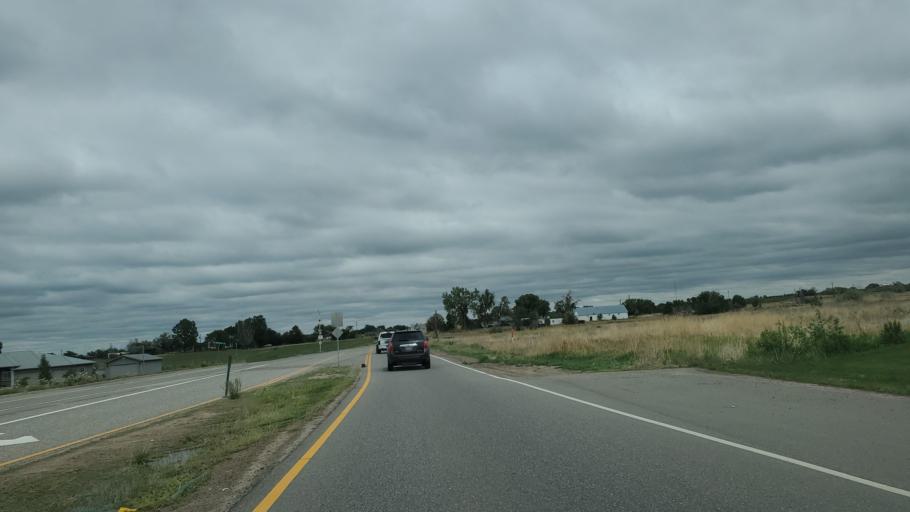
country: US
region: Colorado
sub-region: Adams County
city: Brighton
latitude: 39.9143
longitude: -104.8329
